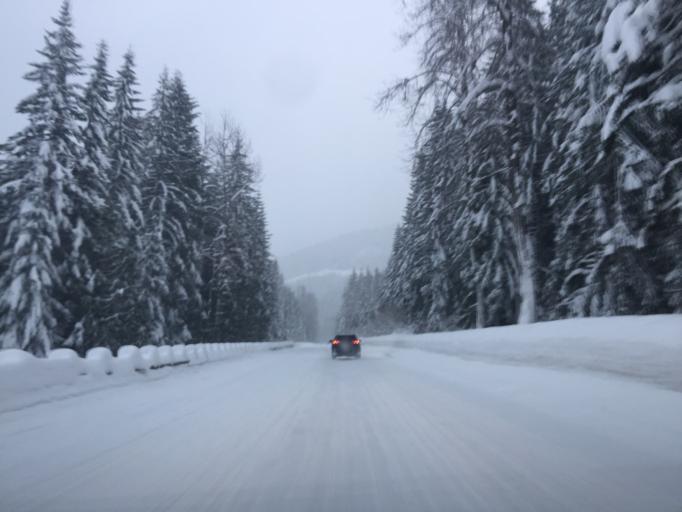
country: US
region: Washington
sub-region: Chelan County
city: Leavenworth
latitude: 47.7764
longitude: -121.0218
